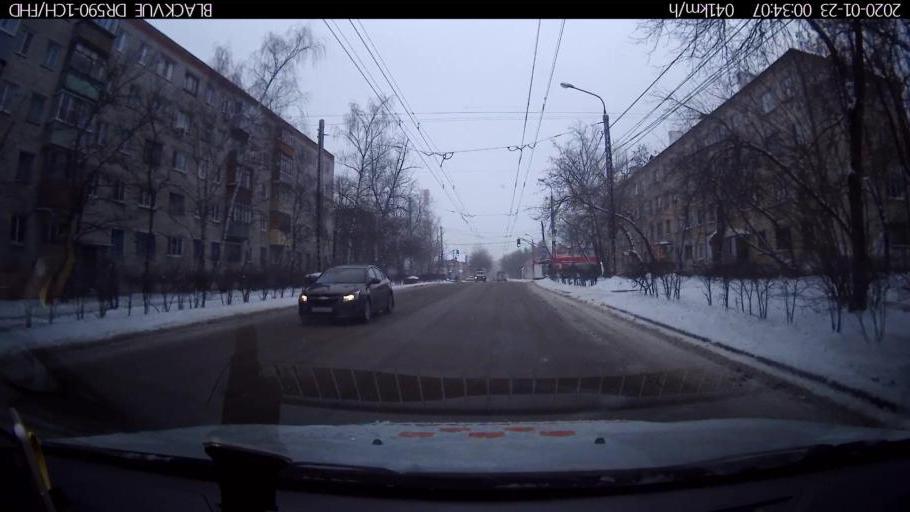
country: RU
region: Nizjnij Novgorod
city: Neklyudovo
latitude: 56.3603
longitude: 43.8477
